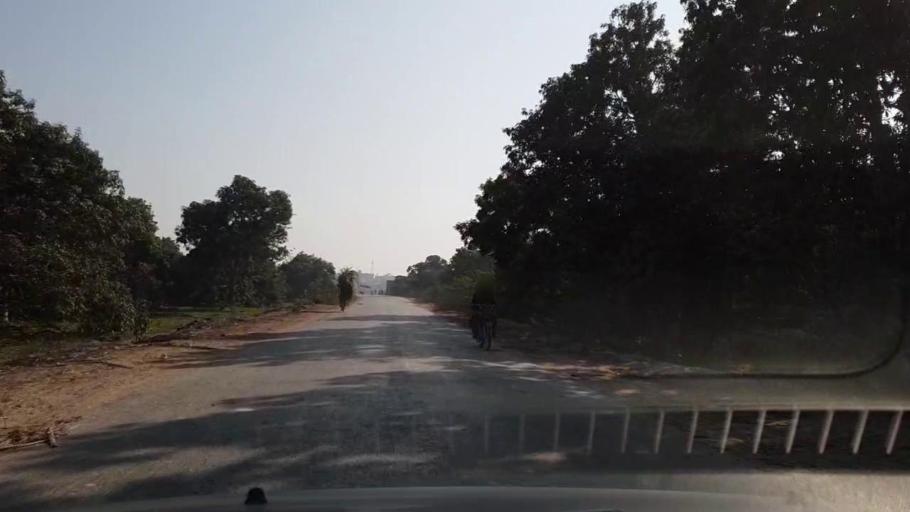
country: PK
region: Sindh
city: Tando Jam
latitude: 25.5178
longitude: 68.6095
